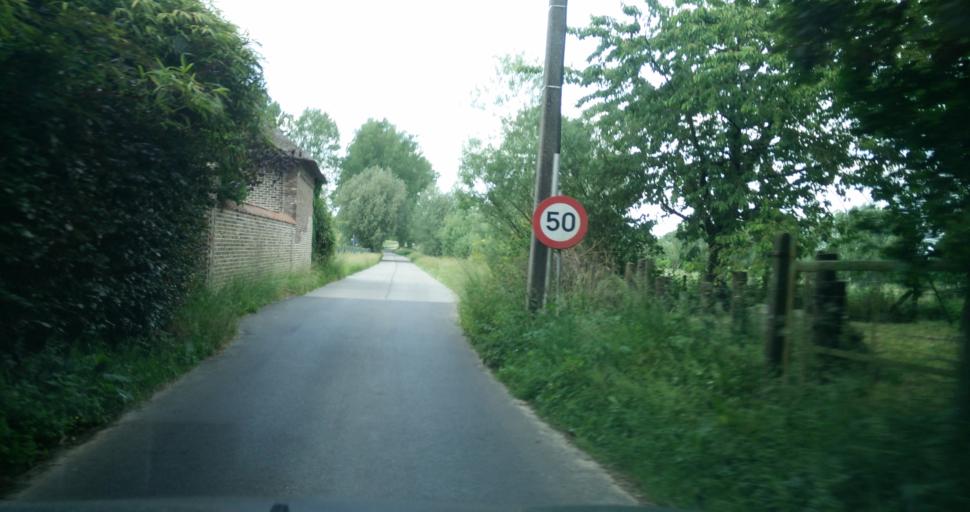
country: BE
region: Wallonia
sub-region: Province du Hainaut
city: Flobecq
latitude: 50.7963
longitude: 3.7425
